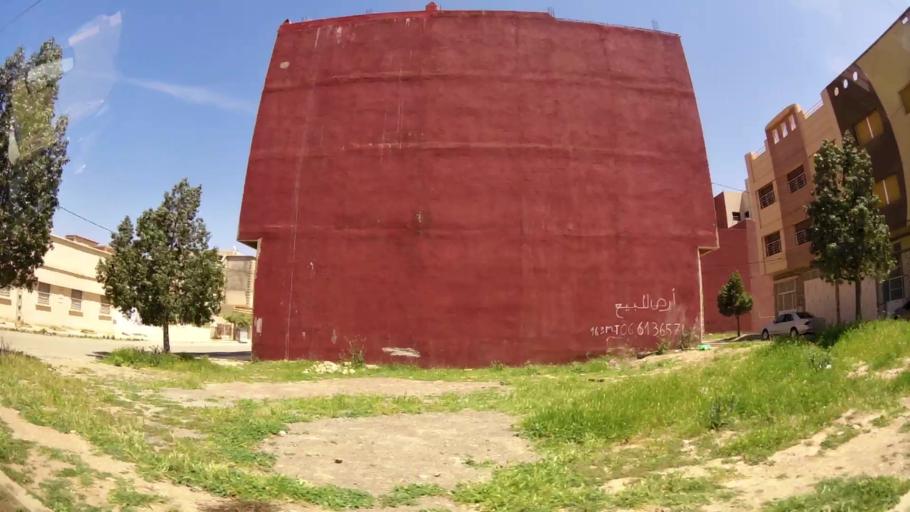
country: MA
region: Oriental
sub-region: Oujda-Angad
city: Oujda
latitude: 34.6849
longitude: -1.9511
